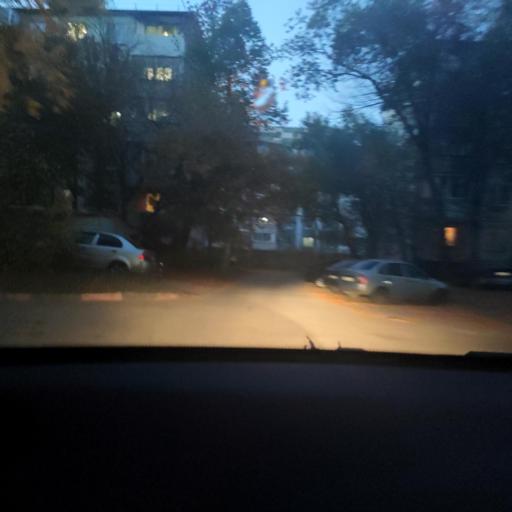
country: RU
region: Samara
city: Samara
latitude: 53.1881
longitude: 50.1965
